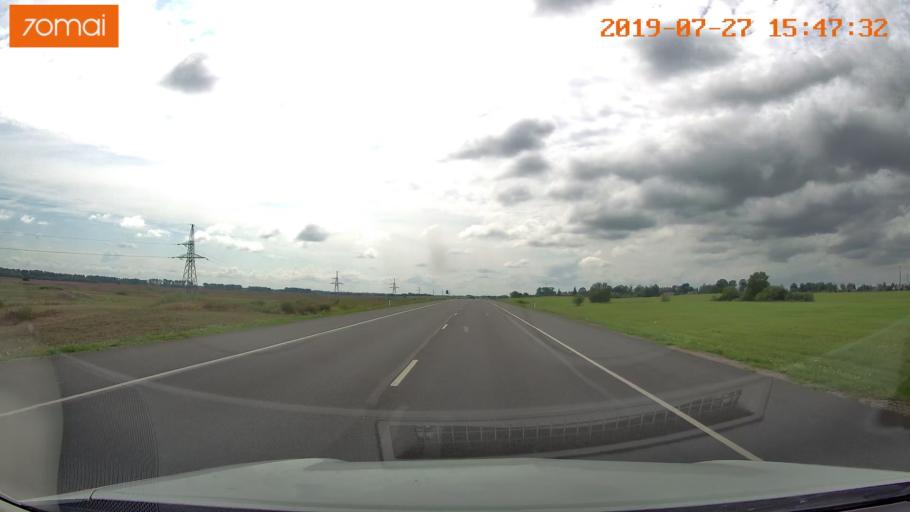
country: RU
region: Kaliningrad
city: Gusev
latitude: 54.6011
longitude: 22.0851
